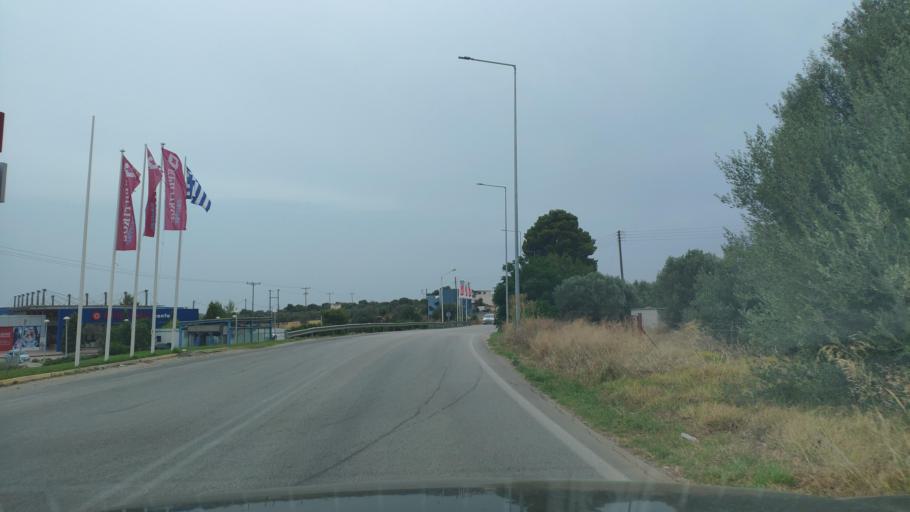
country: GR
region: Peloponnese
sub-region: Nomos Argolidos
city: Porto Cheli
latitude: 37.3430
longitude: 23.1576
